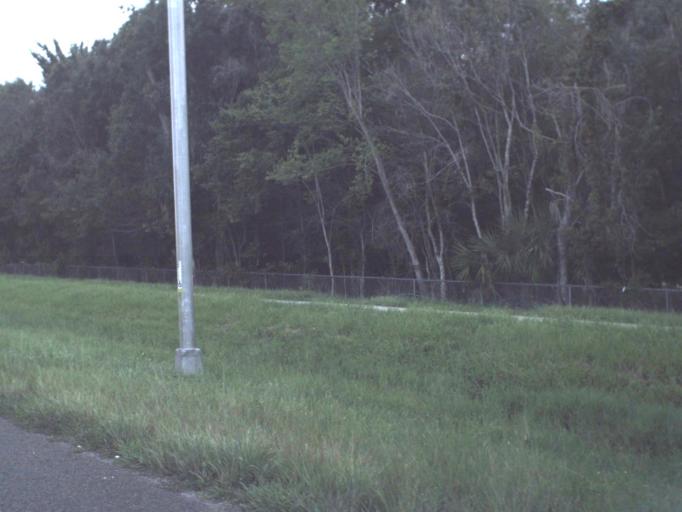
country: US
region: Florida
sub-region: Hillsborough County
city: Temple Terrace
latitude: 28.0250
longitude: -82.3496
